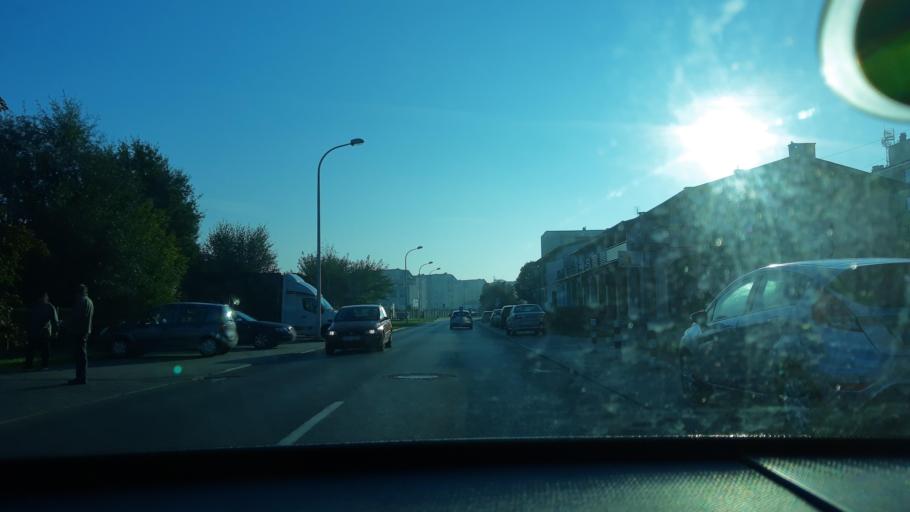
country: PL
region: Lodz Voivodeship
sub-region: Powiat sieradzki
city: Sieradz
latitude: 51.5938
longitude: 18.7216
